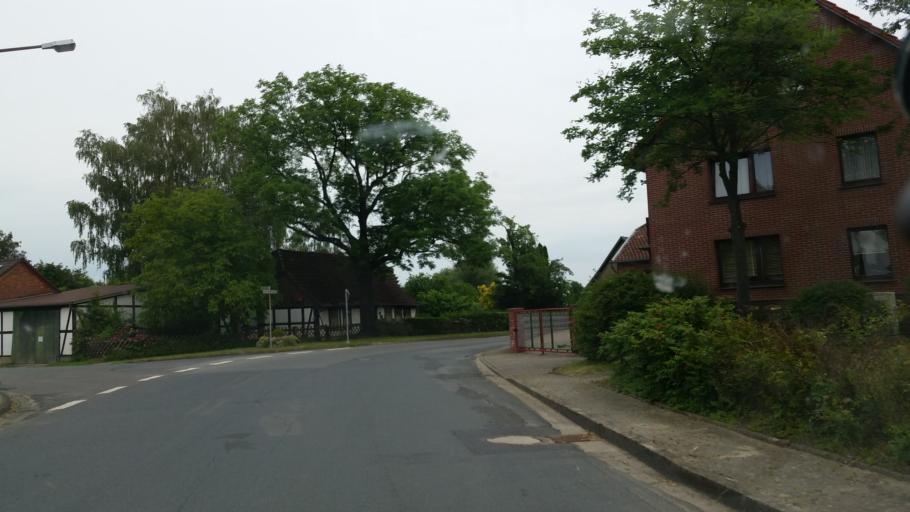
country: DE
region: Lower Saxony
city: Konigslutter am Elm
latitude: 52.2909
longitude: 10.7526
